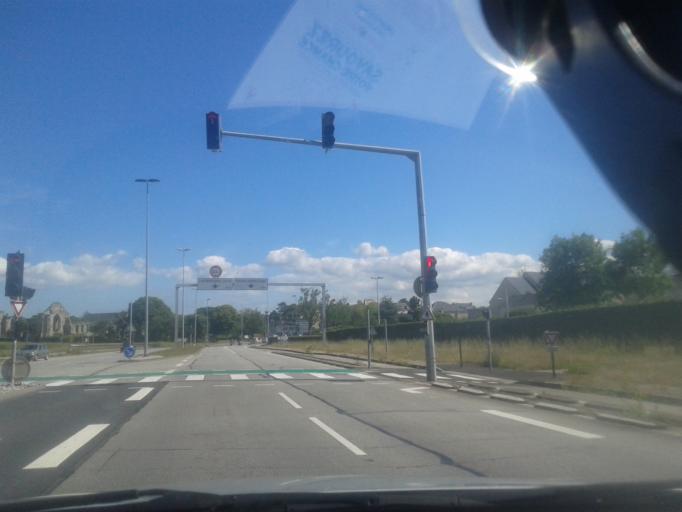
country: FR
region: Lower Normandy
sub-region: Departement de la Manche
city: Equeurdreville-Hainneville
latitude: 49.6490
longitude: -1.6443
